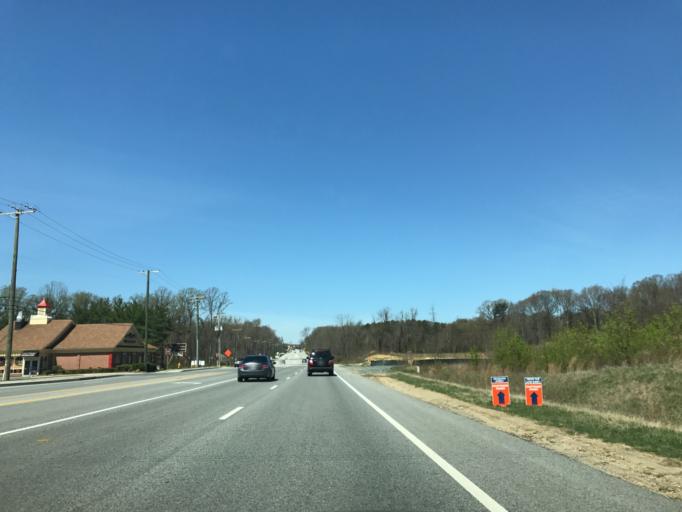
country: US
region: Maryland
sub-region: Anne Arundel County
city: Fort Meade
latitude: 39.1322
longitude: -76.7408
